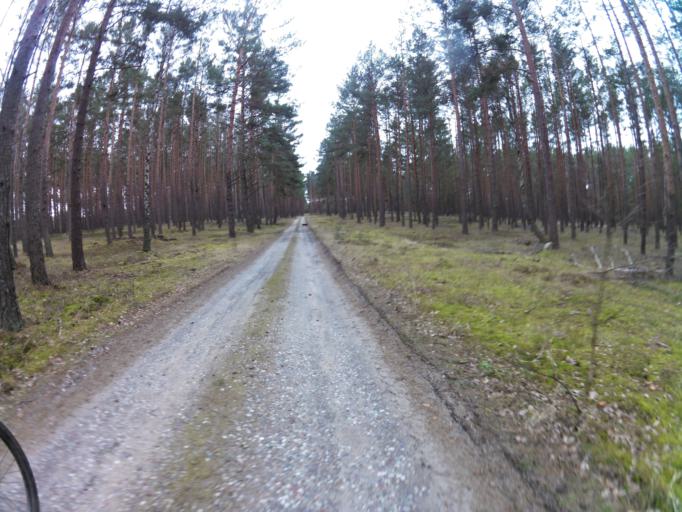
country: PL
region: West Pomeranian Voivodeship
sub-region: Powiat mysliborski
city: Debno
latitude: 52.7553
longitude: 14.7853
